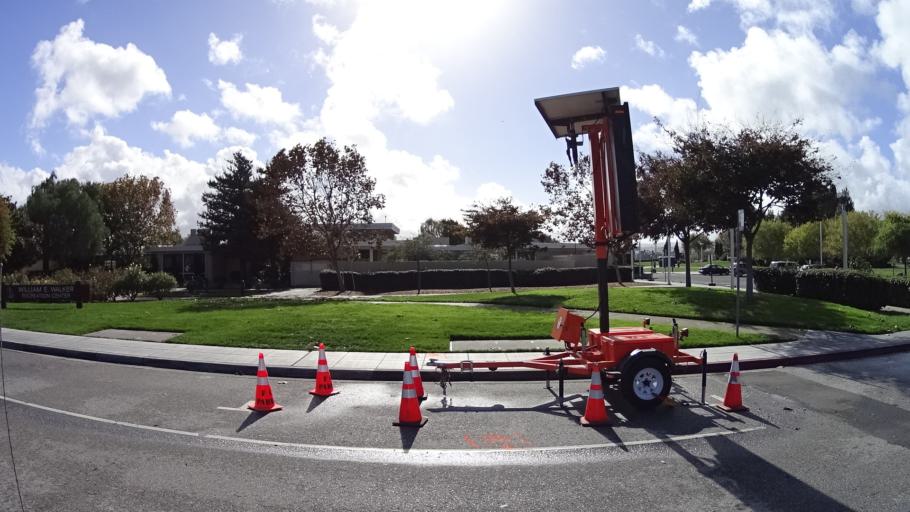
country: US
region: California
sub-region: San Mateo County
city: Foster City
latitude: 37.5578
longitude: -122.2700
